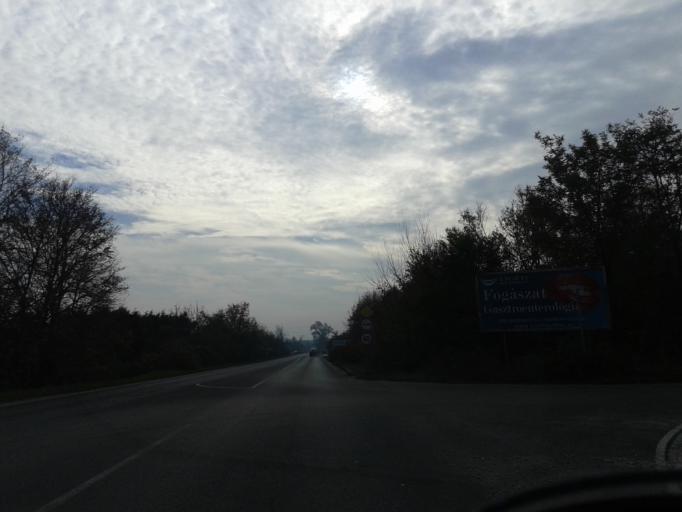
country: HU
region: Budapest
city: Budapest XXII. keruelet
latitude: 47.4351
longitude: 19.0063
